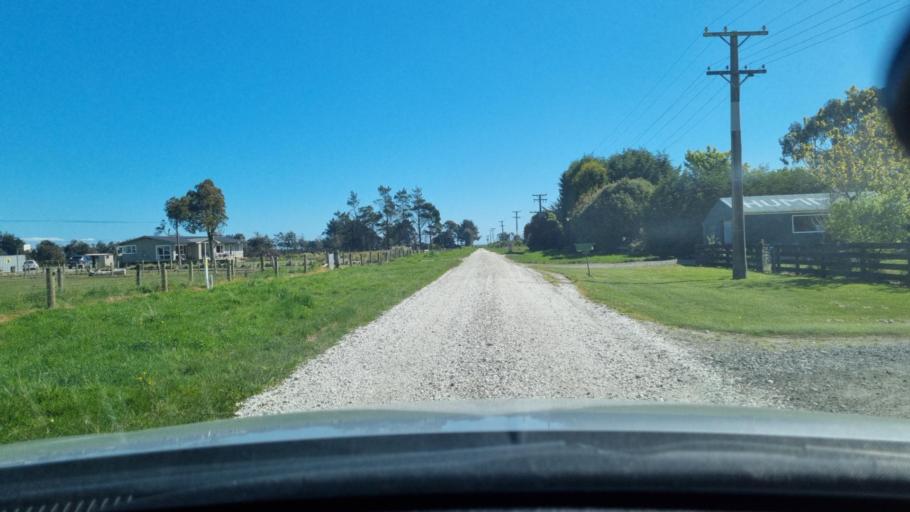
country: NZ
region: Southland
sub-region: Invercargill City
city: Invercargill
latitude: -46.3910
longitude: 168.2975
